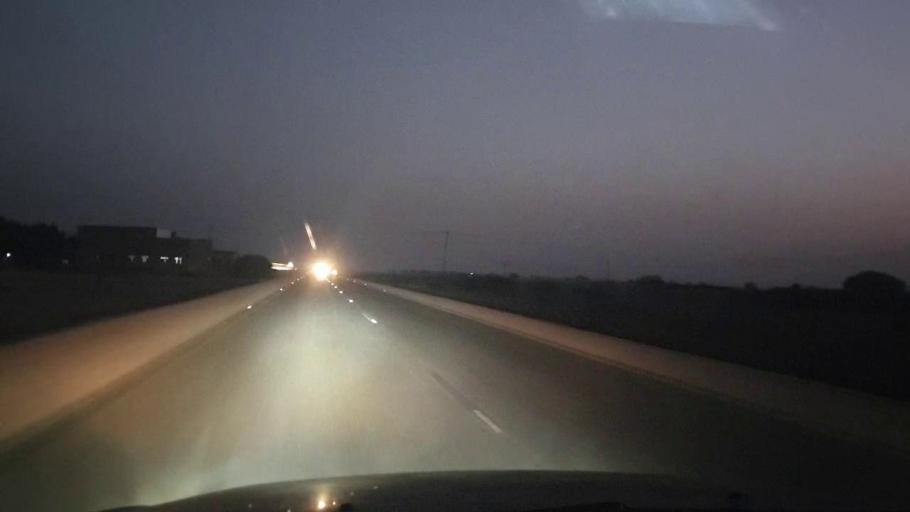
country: PK
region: Sindh
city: Chambar
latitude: 25.3454
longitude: 68.7923
